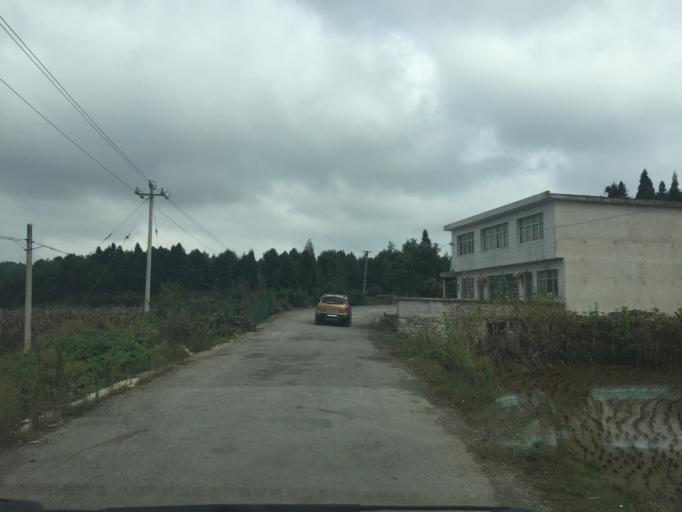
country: CN
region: Guizhou Sheng
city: Guiyang
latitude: 26.8950
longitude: 107.1722
